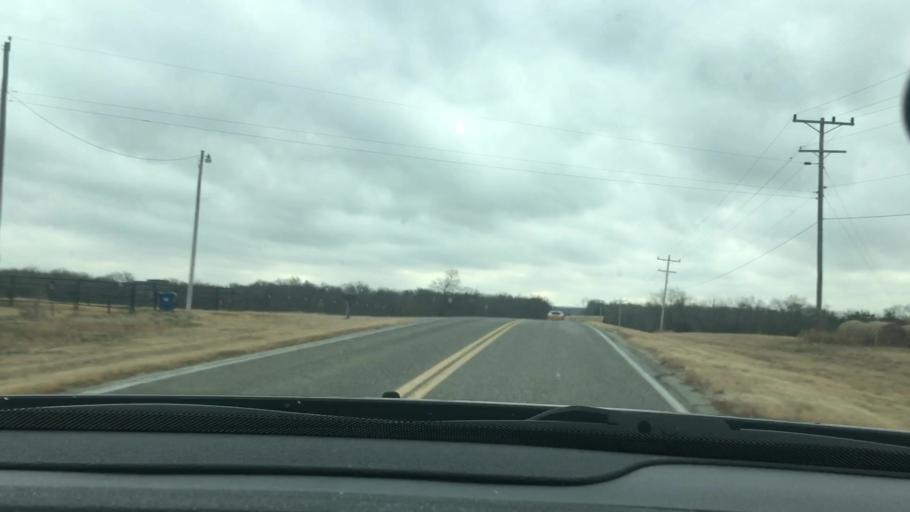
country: US
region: Oklahoma
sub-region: Johnston County
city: Tishomingo
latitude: 34.1519
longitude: -96.5574
